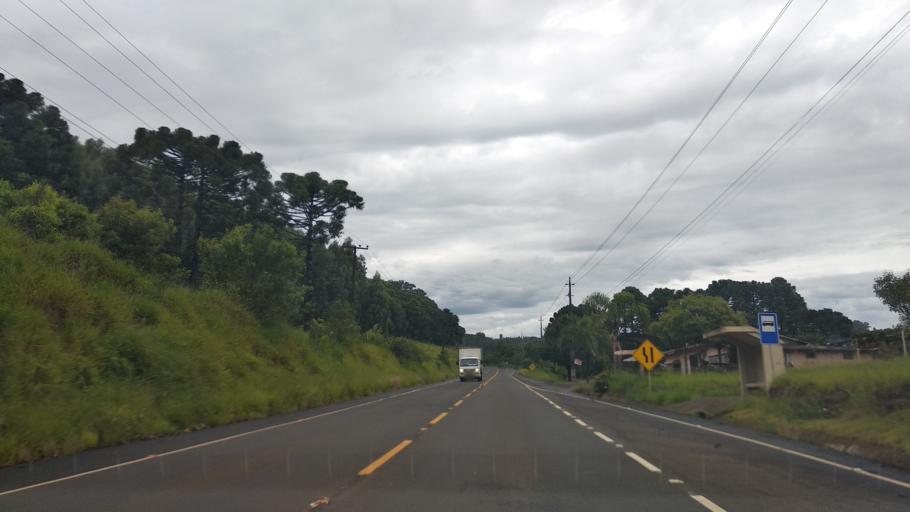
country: BR
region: Santa Catarina
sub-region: Videira
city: Videira
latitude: -27.0483
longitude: -51.1675
